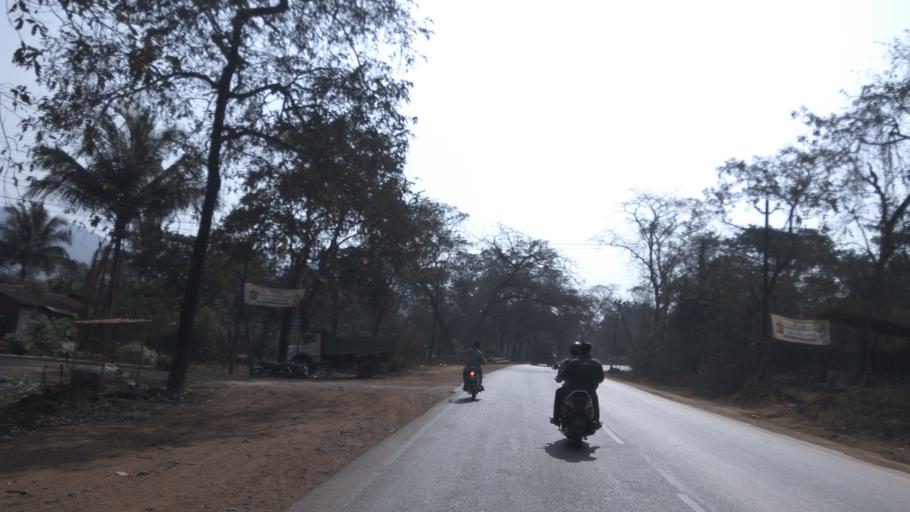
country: IN
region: Goa
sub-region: North Goa
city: Palle
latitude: 15.4101
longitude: 74.0887
